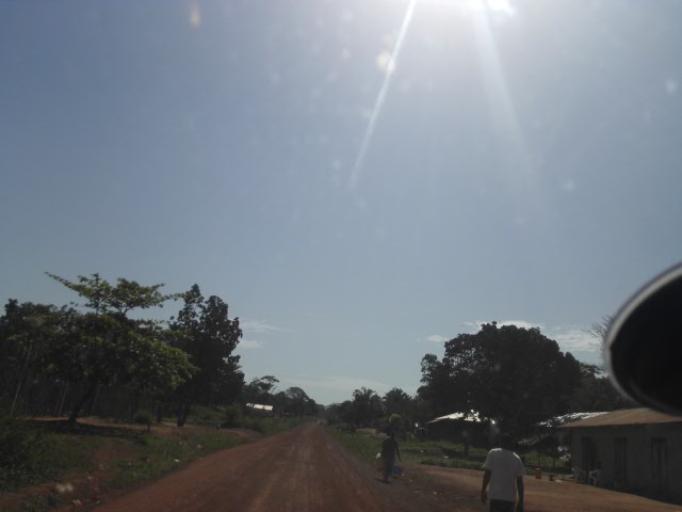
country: CD
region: Eastern Province
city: Wamba
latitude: 1.4095
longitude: 28.0833
